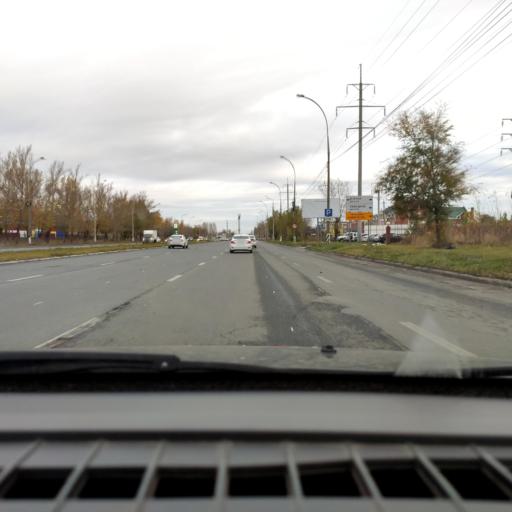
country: RU
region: Samara
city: Tol'yatti
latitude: 53.5470
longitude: 49.2855
